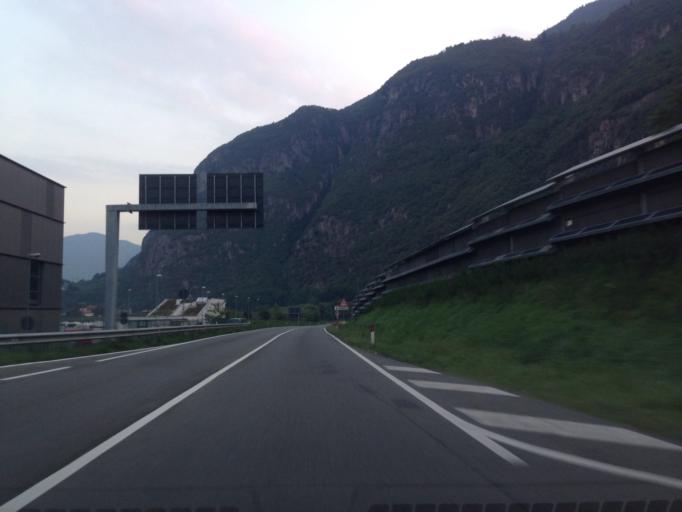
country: IT
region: Trentino-Alto Adige
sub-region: Bolzano
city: Pineta
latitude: 46.4448
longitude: 11.3432
